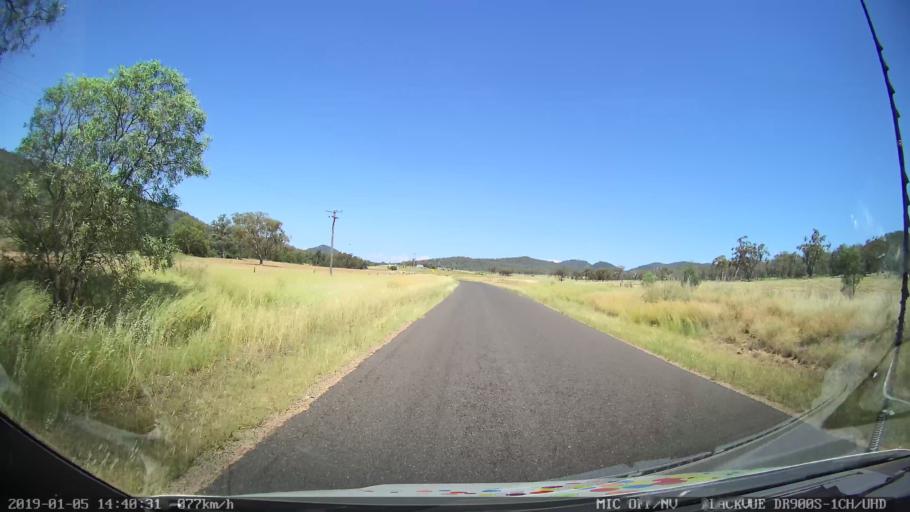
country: AU
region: New South Wales
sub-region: Tamworth Municipality
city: Phillip
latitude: -31.2593
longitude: 150.7138
